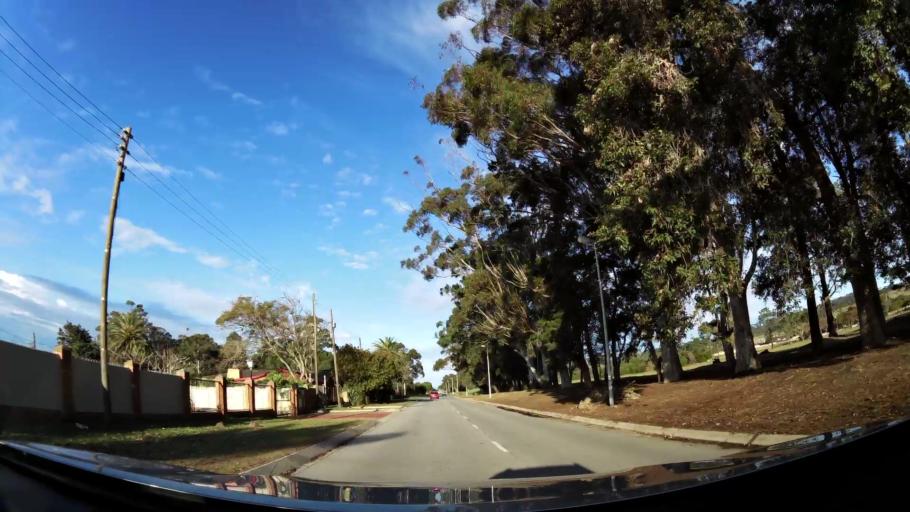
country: ZA
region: Eastern Cape
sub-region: Nelson Mandela Bay Metropolitan Municipality
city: Port Elizabeth
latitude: -33.9753
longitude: 25.5064
